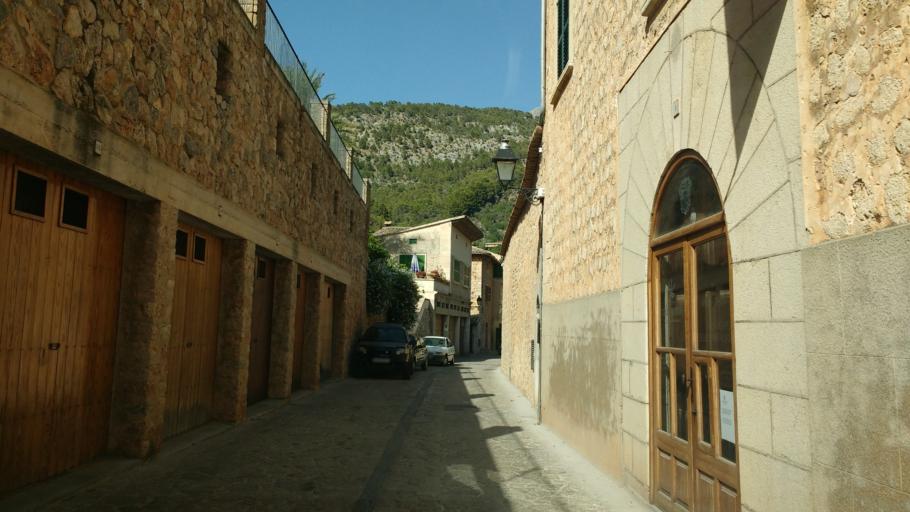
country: ES
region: Balearic Islands
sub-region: Illes Balears
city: Fornalutx
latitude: 39.7827
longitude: 2.7418
